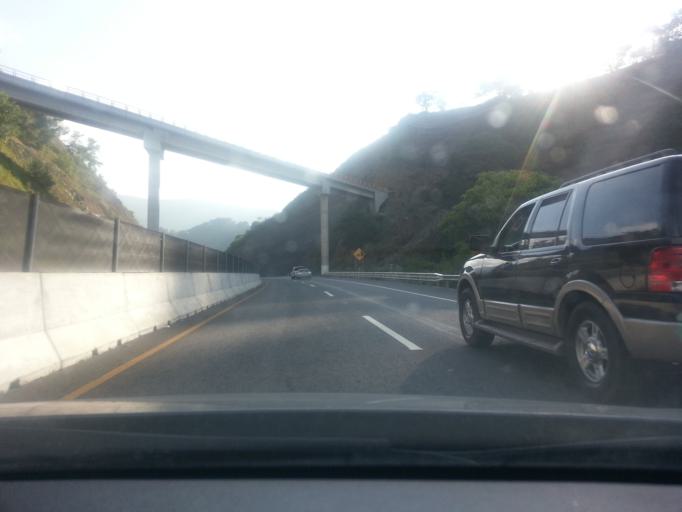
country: MX
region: Puebla
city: Necaxa
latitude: 20.2509
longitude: -98.0302
